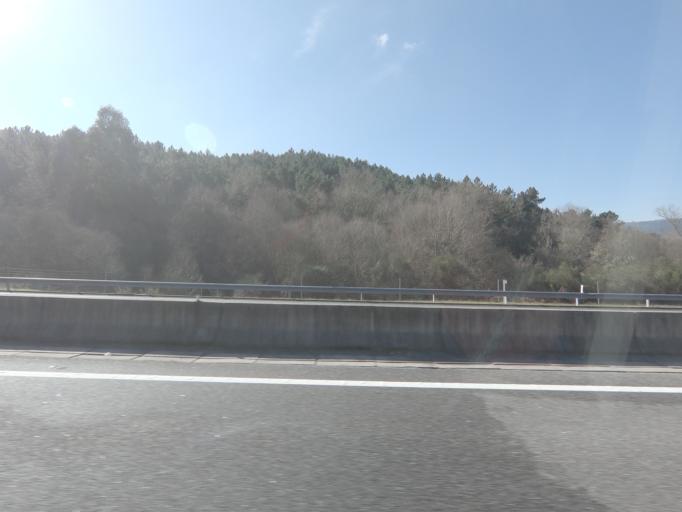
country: ES
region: Galicia
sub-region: Provincia de Ourense
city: Cea
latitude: 42.4594
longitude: -8.0236
